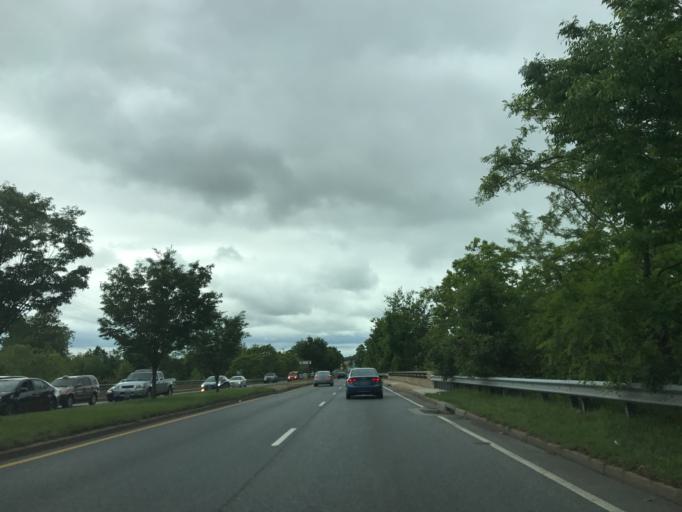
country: US
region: Maryland
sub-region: Prince George's County
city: East Riverdale
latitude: 38.9614
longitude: -76.9241
